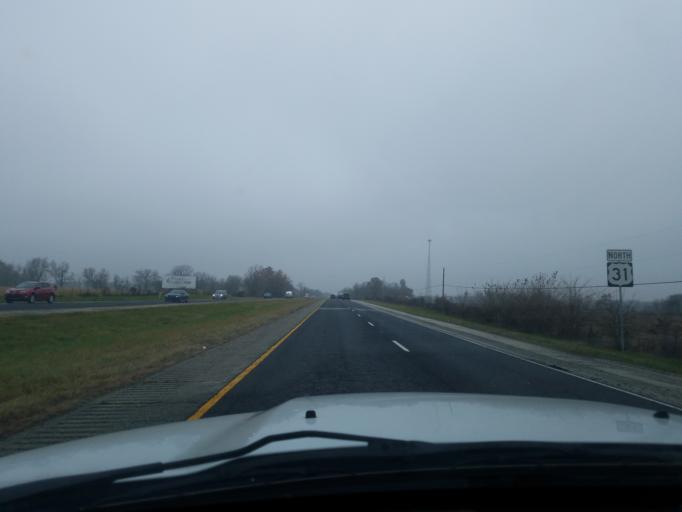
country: US
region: Indiana
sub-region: Hamilton County
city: Westfield
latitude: 40.1171
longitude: -86.1279
